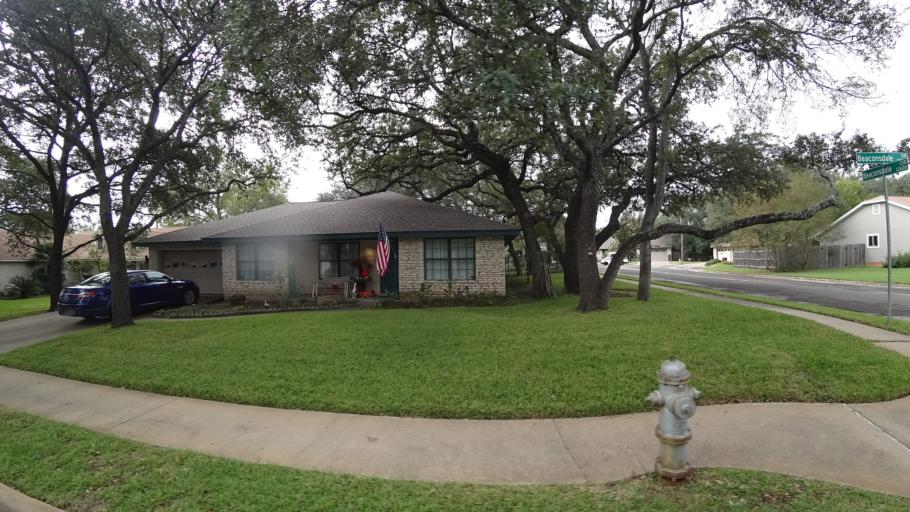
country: US
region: Texas
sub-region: Travis County
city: Wells Branch
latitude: 30.4260
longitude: -97.7133
